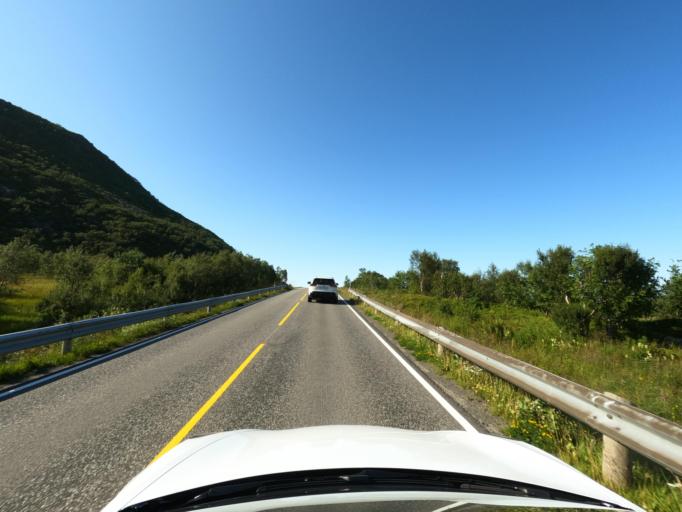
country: NO
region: Nordland
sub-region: Vagan
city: Kabelvag
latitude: 68.2758
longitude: 14.1370
